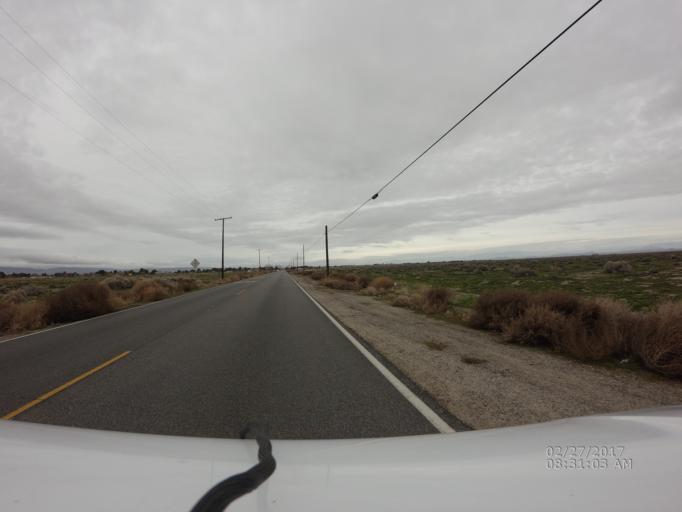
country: US
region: California
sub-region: Los Angeles County
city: Lancaster
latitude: 34.7045
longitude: -118.0436
